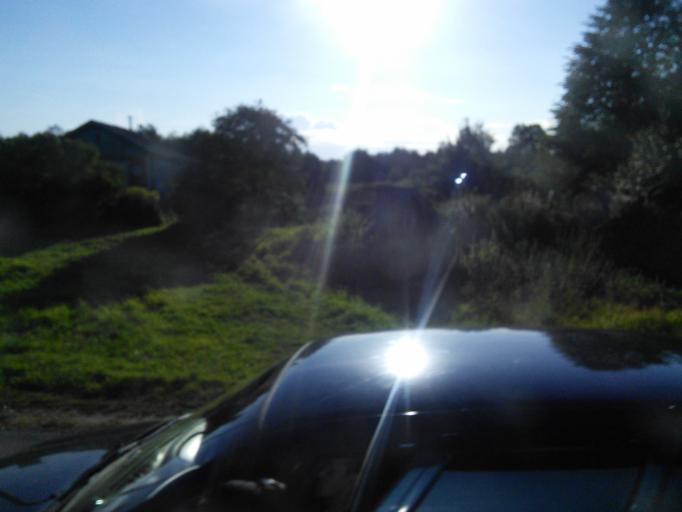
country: RU
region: Jaroslavl
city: Poshekhon'ye
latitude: 58.4535
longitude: 39.0345
